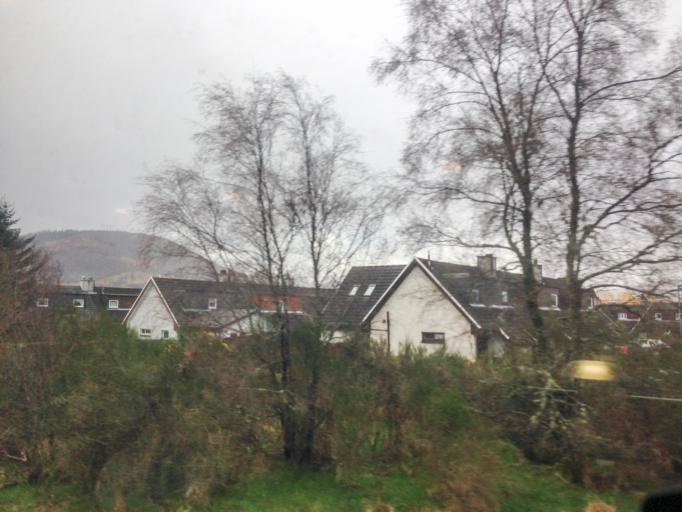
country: GB
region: Scotland
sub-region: Highland
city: Fort William
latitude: 56.8361
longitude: -5.0848
